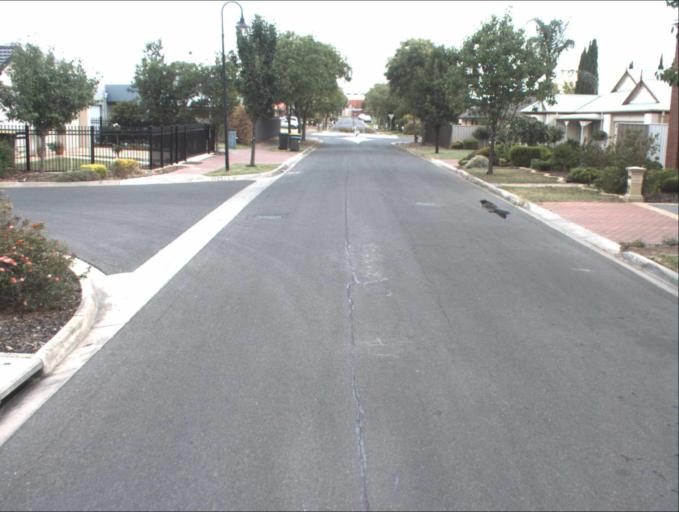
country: AU
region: South Australia
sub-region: Port Adelaide Enfield
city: Gilles Plains
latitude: -34.8506
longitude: 138.6331
